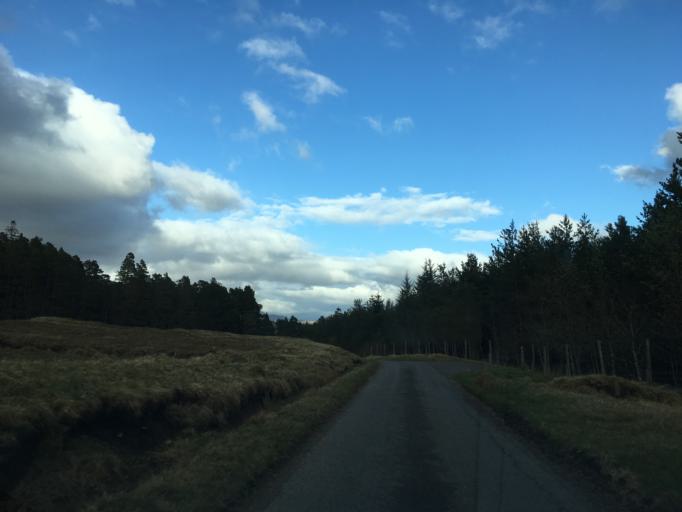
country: GB
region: Scotland
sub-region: Highland
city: Kingussie
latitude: 57.0095
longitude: -4.3963
